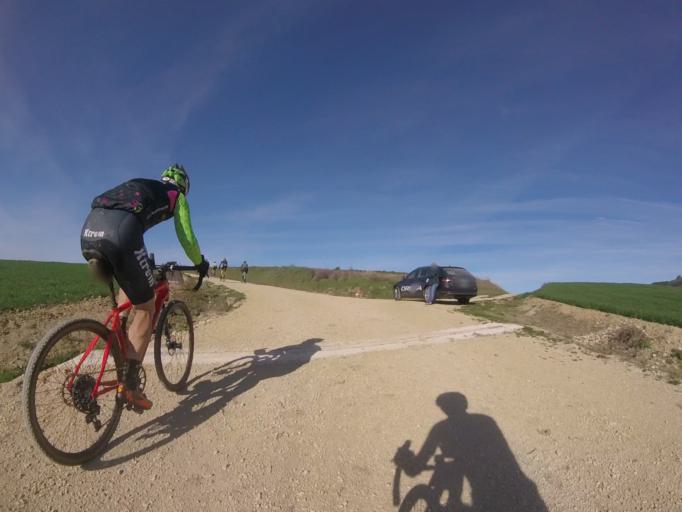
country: ES
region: Navarre
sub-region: Provincia de Navarra
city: Yerri
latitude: 42.7204
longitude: -1.9651
